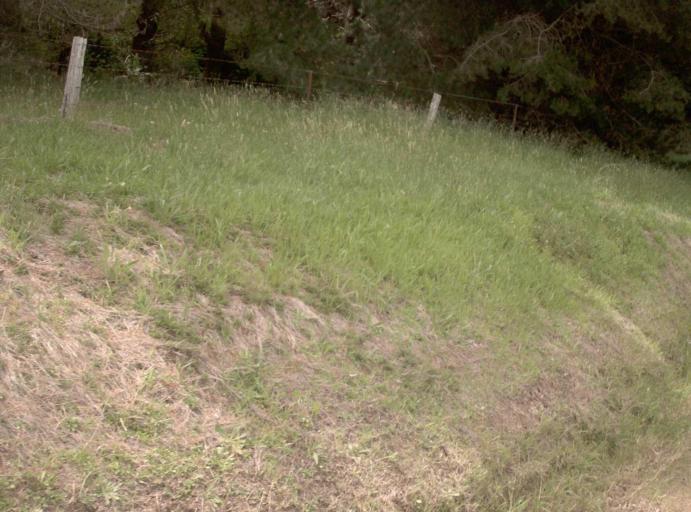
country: AU
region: Victoria
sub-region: Latrobe
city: Traralgon
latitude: -38.4090
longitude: 146.6335
